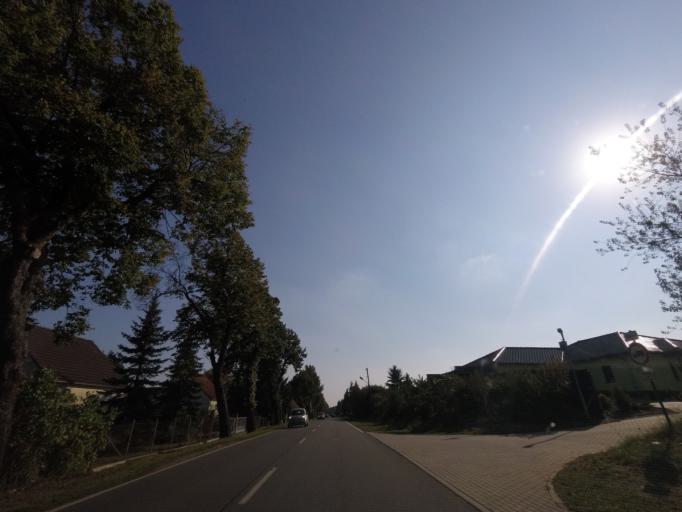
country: DE
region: Saxony-Anhalt
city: Jessen
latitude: 51.8023
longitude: 13.0163
